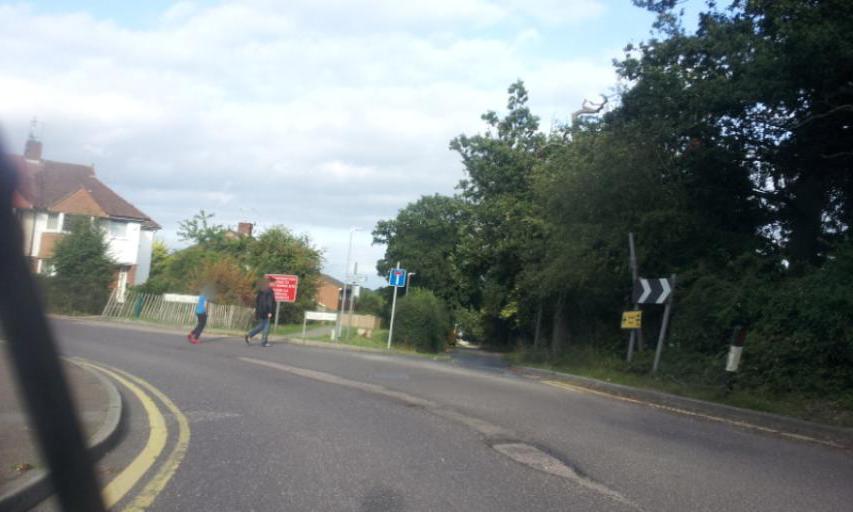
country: GB
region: England
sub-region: Kent
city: Tonbridge
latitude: 51.1849
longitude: 0.2836
